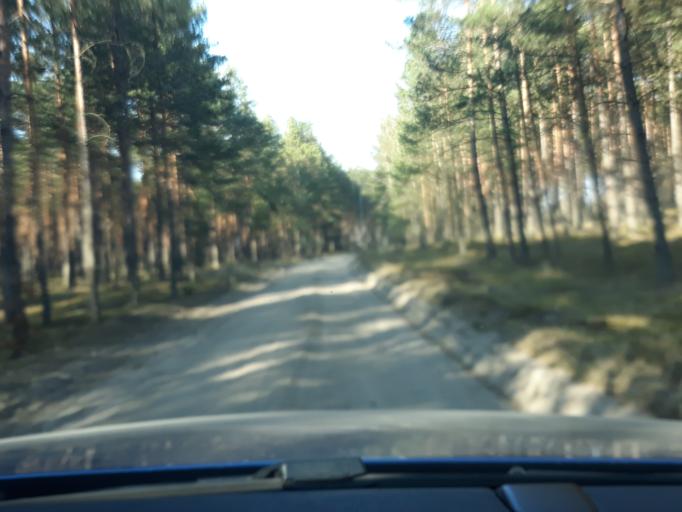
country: PL
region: Pomeranian Voivodeship
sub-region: Powiat bytowski
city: Lipnica
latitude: 53.9208
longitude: 17.4414
